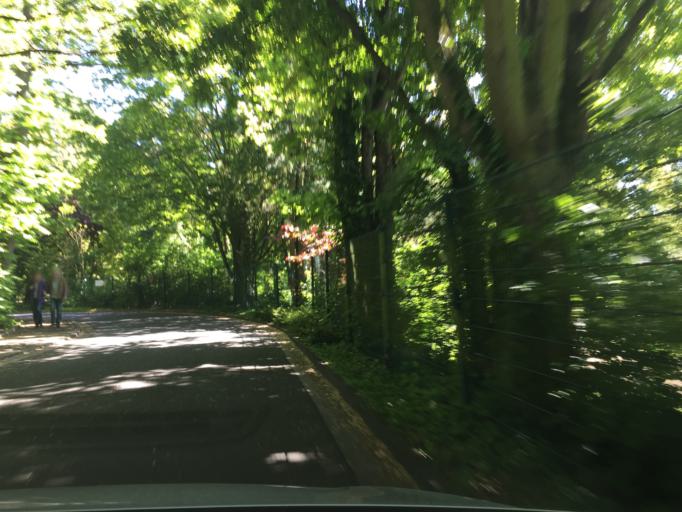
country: DE
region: Hesse
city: Niederrad
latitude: 50.0906
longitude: 8.6470
